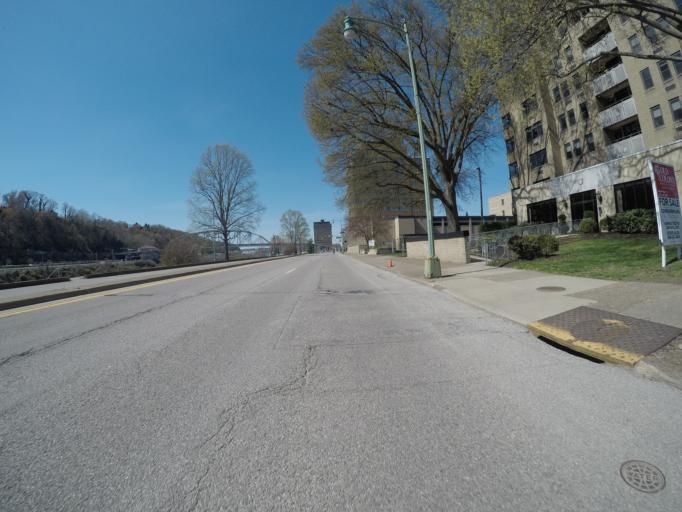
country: US
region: West Virginia
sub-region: Kanawha County
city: Charleston
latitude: 38.3453
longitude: -81.6335
